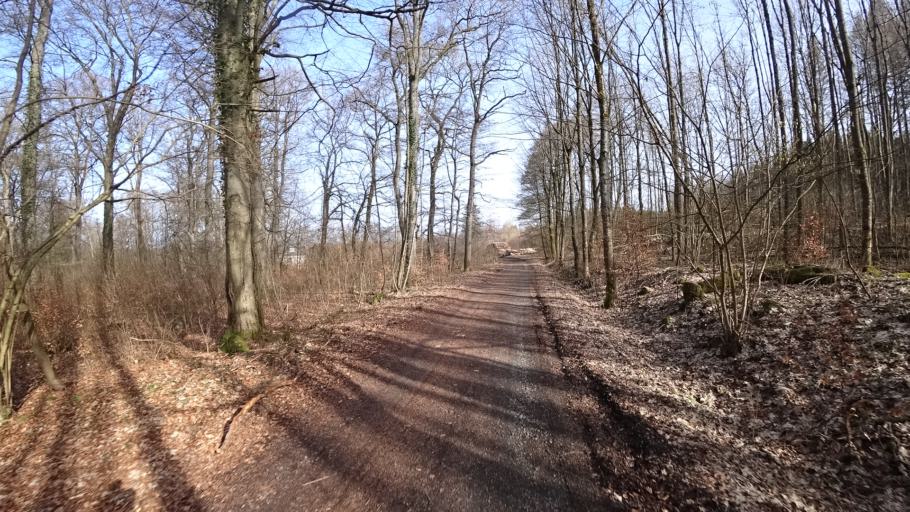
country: DE
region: Rheinland-Pfalz
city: Dickendorf
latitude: 50.7251
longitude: 7.8527
